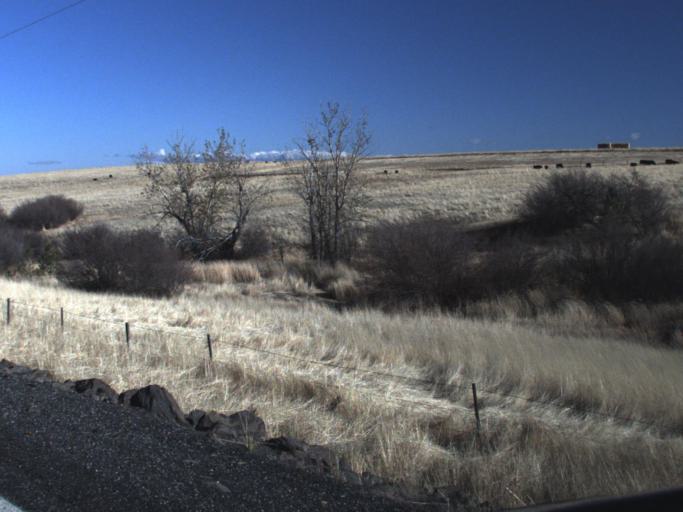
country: US
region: Washington
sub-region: Asotin County
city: Asotin
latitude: 46.1397
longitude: -117.1290
